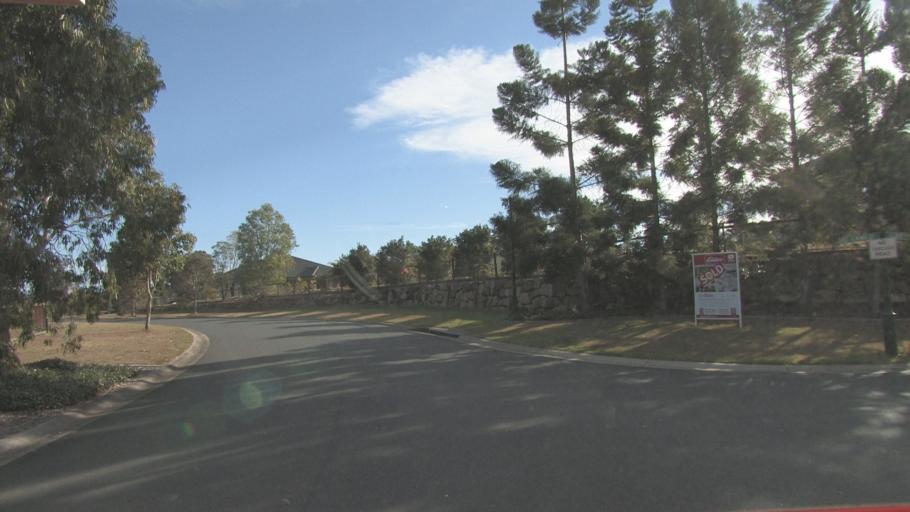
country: AU
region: Queensland
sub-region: Logan
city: North Maclean
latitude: -27.7980
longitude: 152.9632
